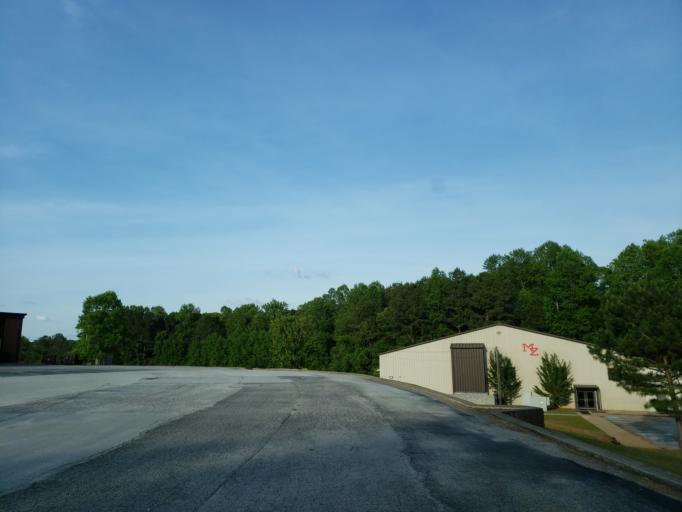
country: US
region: Georgia
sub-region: Carroll County
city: Mount Zion
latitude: 33.6370
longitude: -85.1845
